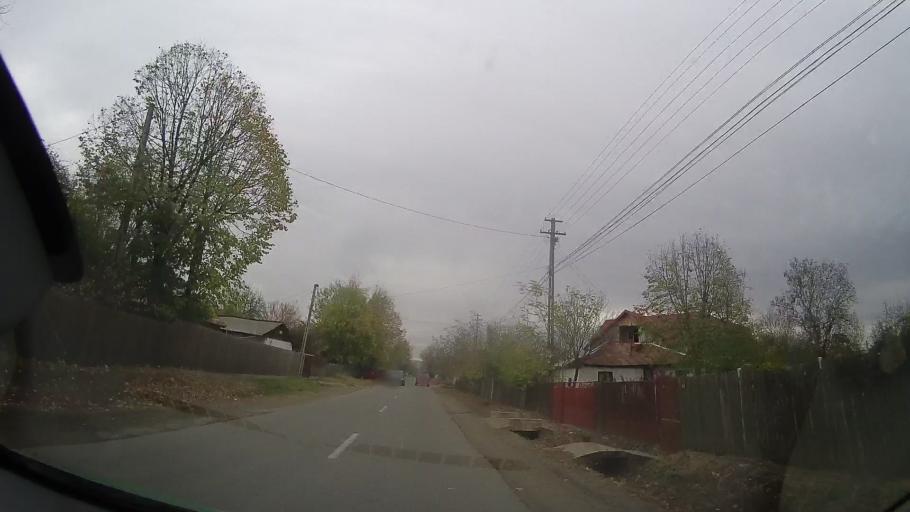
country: RO
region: Prahova
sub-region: Comuna Fantanele
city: Fantanele
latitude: 45.0103
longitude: 26.3783
